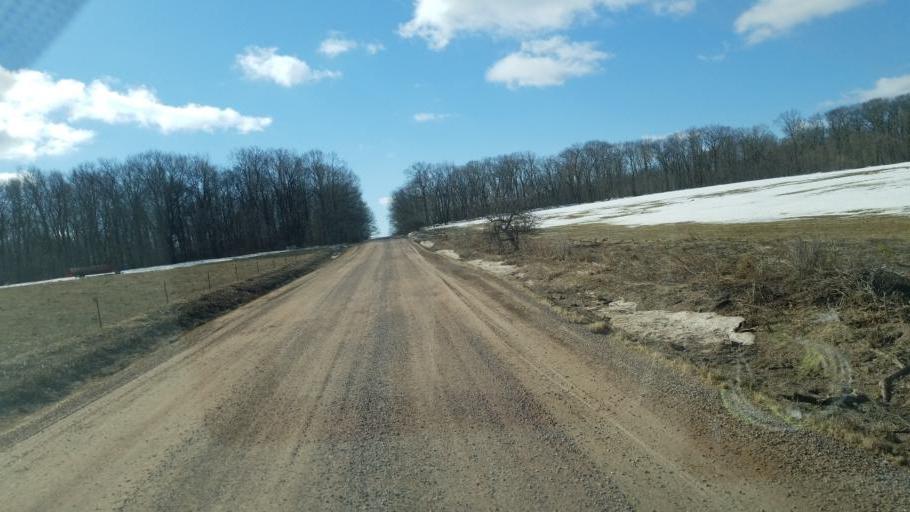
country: US
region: Wisconsin
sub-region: Clark County
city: Loyal
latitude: 44.6640
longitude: -90.4560
